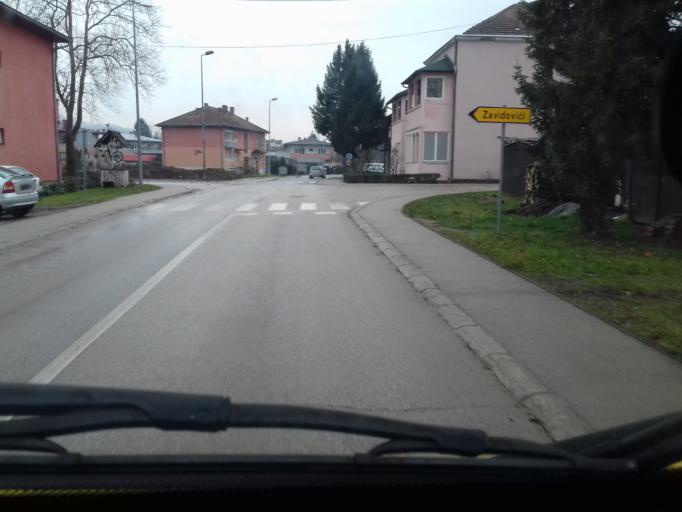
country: BA
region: Federation of Bosnia and Herzegovina
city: Maglaj
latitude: 44.5497
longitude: 18.0958
